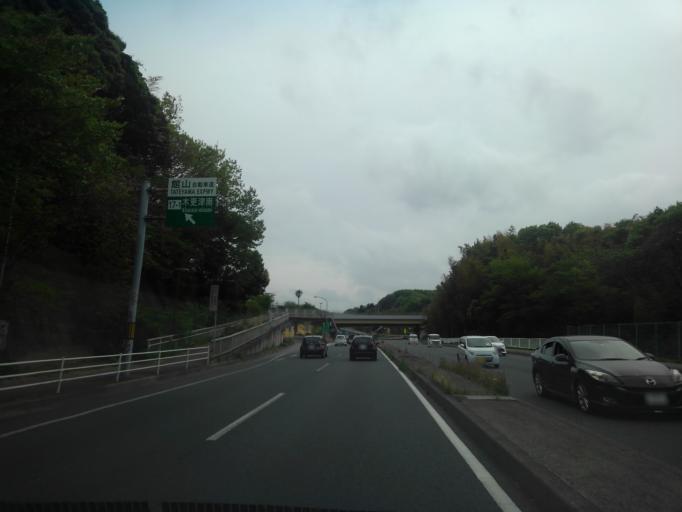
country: JP
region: Chiba
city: Kisarazu
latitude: 35.3520
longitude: 139.9203
